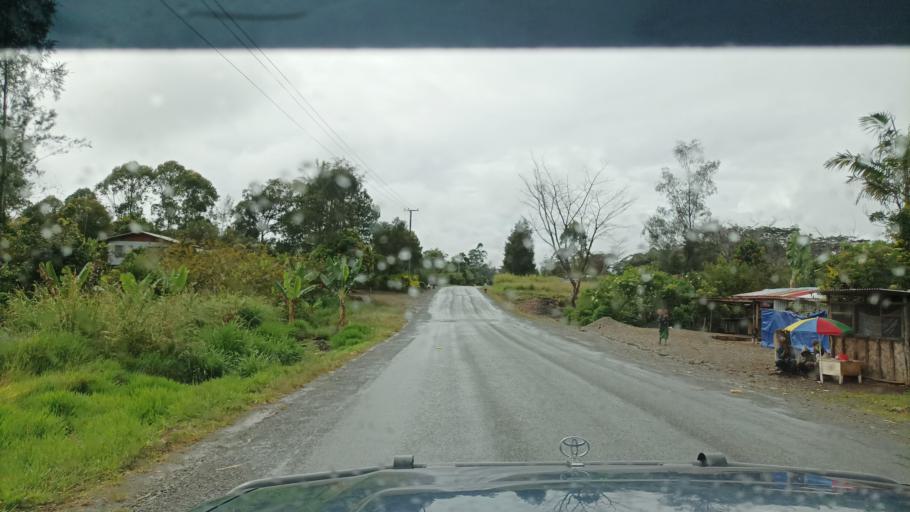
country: PG
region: Jiwaka
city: Minj
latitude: -5.8742
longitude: 144.6633
